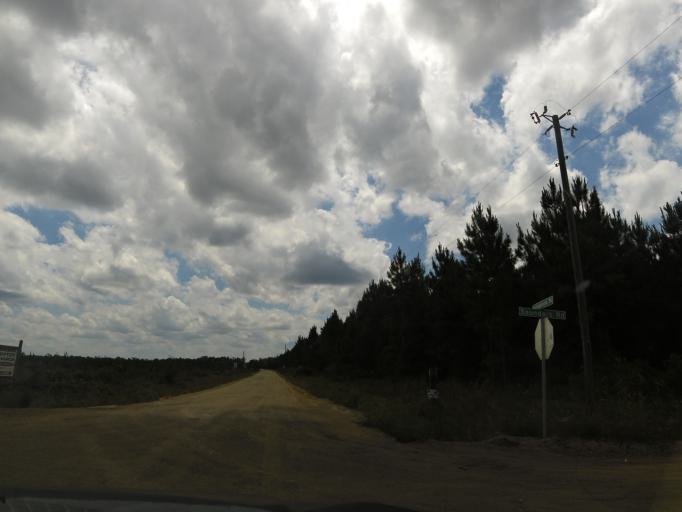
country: US
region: Florida
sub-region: Clay County
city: Green Cove Springs
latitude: 29.9148
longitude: -81.7806
